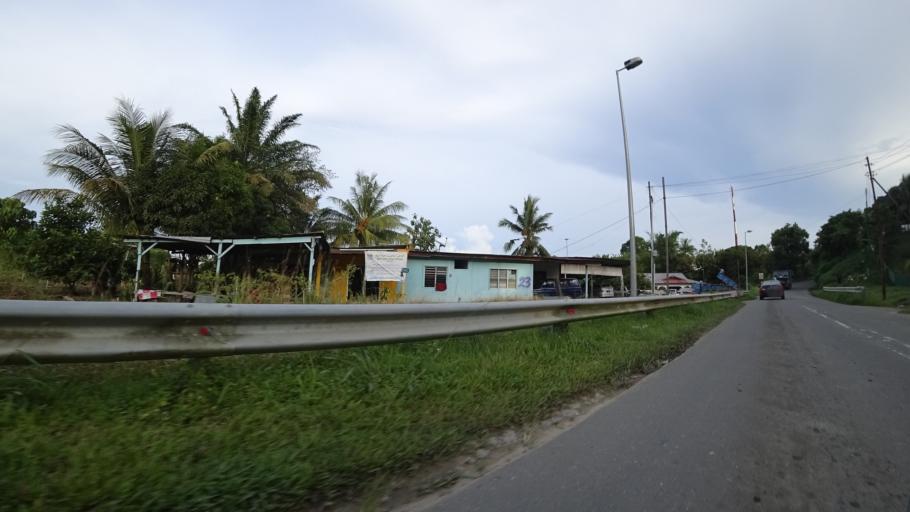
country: BN
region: Brunei and Muara
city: Bandar Seri Begawan
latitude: 4.8644
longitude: 114.8206
